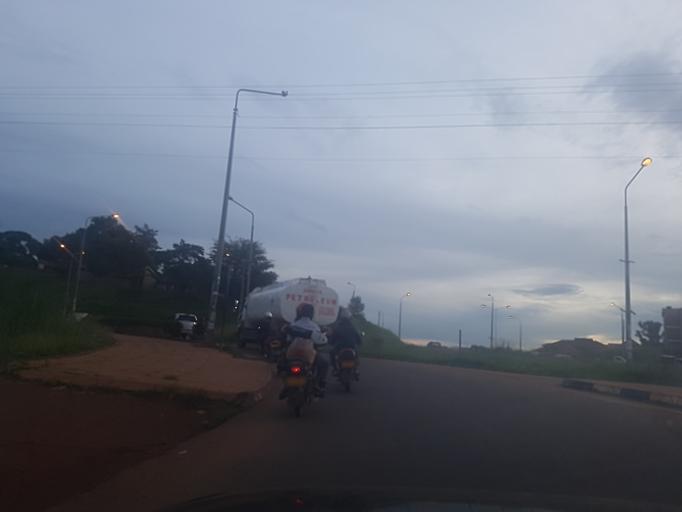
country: UG
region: Central Region
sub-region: Wakiso District
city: Kireka
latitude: 0.3657
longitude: 32.6054
